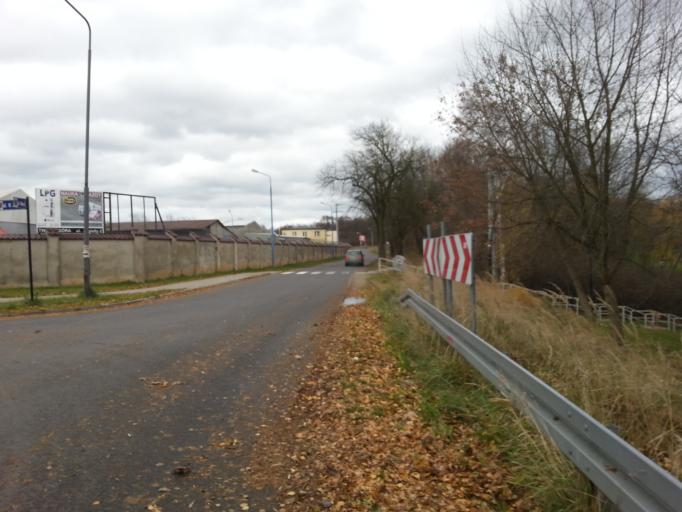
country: PL
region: Lower Silesian Voivodeship
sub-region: Powiat olesnicki
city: Twardogora
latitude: 51.3647
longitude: 17.4727
